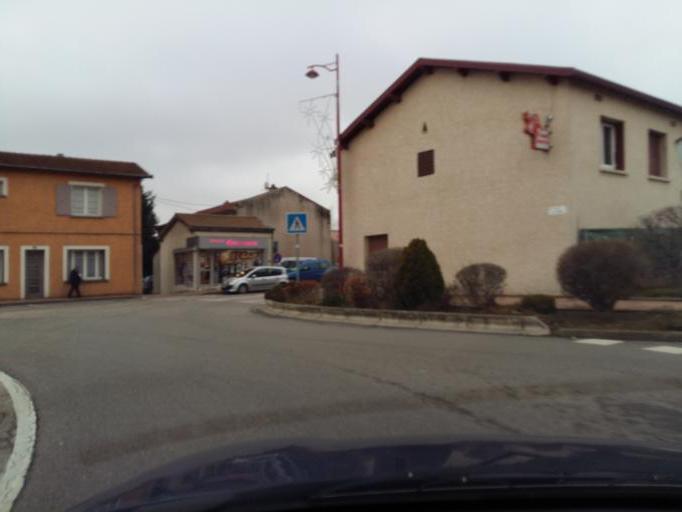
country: FR
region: Rhone-Alpes
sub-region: Departement de l'Ardeche
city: Davezieux
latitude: 45.2556
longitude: 4.7073
